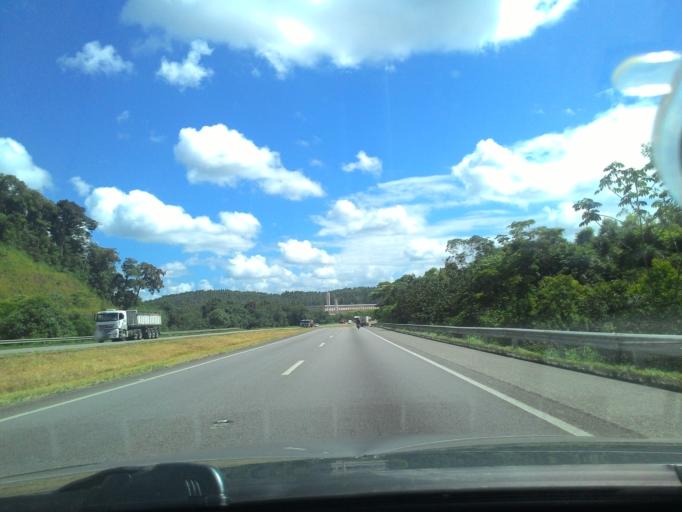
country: BR
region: Sao Paulo
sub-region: Registro
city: Registro
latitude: -24.5590
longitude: -47.8667
